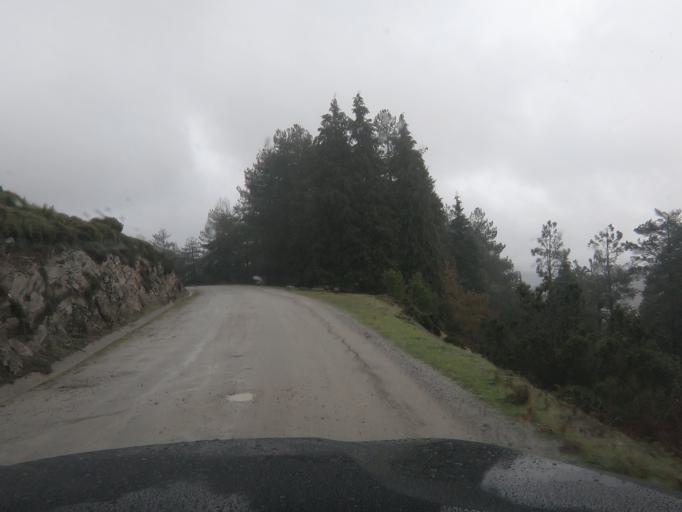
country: PT
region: Vila Real
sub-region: Mondim de Basto
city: Mondim de Basto
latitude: 41.3205
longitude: -7.8734
